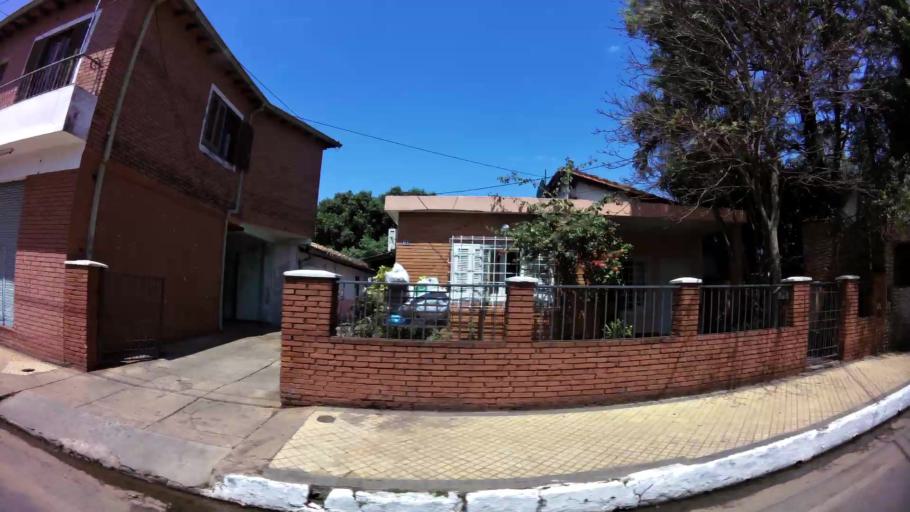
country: PY
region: Central
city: Fernando de la Mora
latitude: -25.3259
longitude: -57.5561
